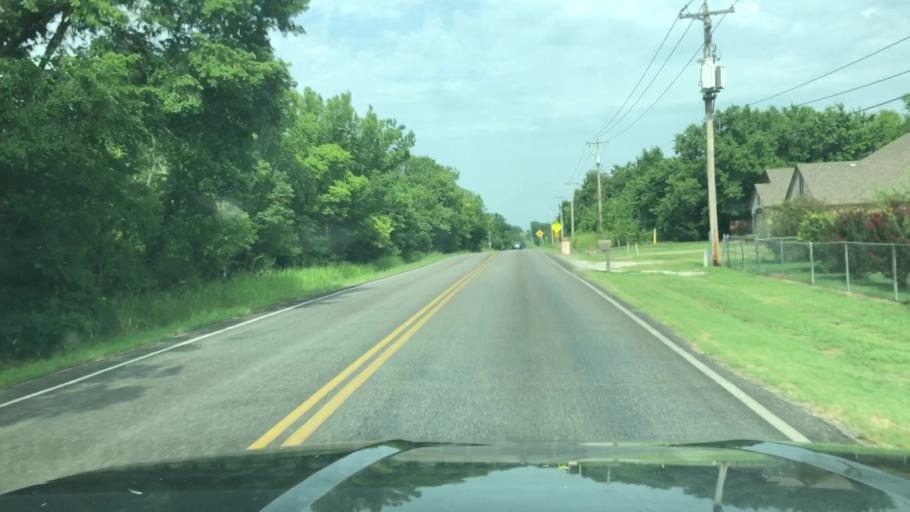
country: US
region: Oklahoma
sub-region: Tulsa County
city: Sand Springs
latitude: 36.0901
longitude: -96.1153
